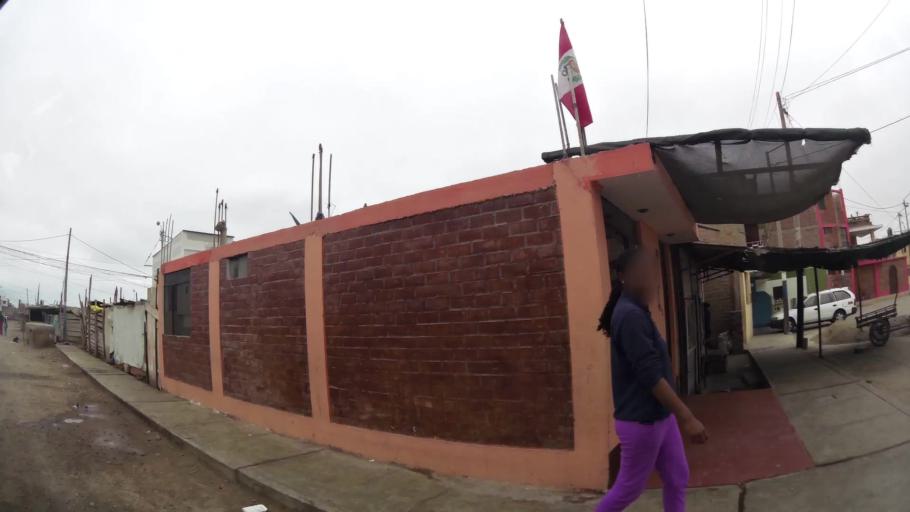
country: PE
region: Ica
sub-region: Provincia de Pisco
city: Pisco
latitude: -13.7055
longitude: -76.2025
